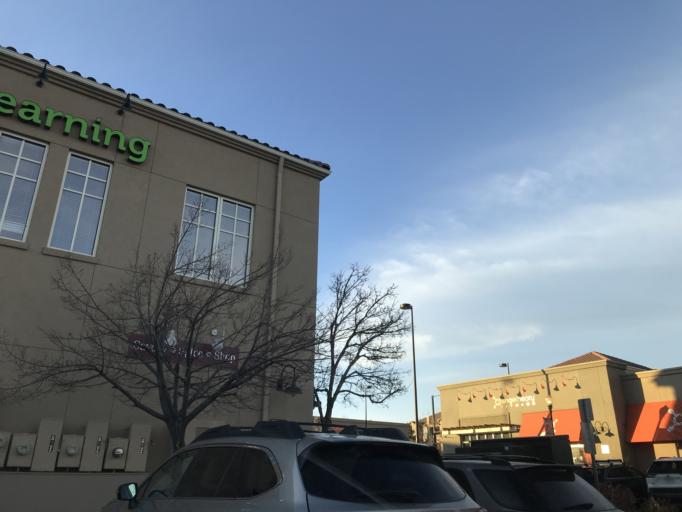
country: US
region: Colorado
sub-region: Arapahoe County
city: Glendale
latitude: 39.7207
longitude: -104.9028
